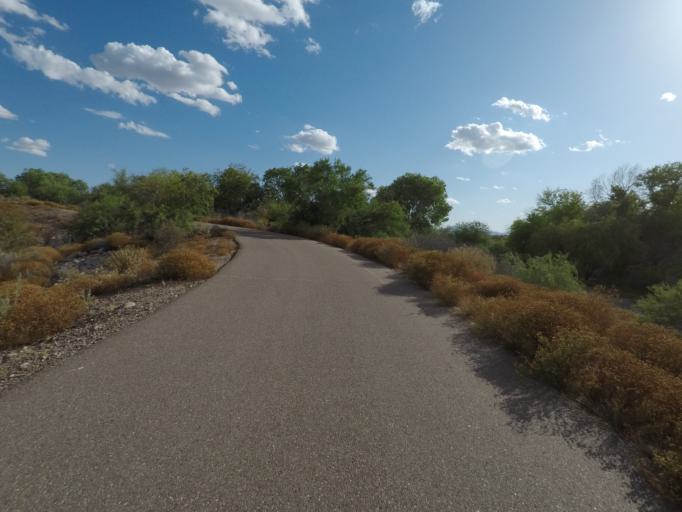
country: US
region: Arizona
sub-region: Maricopa County
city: Phoenix
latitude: 33.4175
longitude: -112.0832
